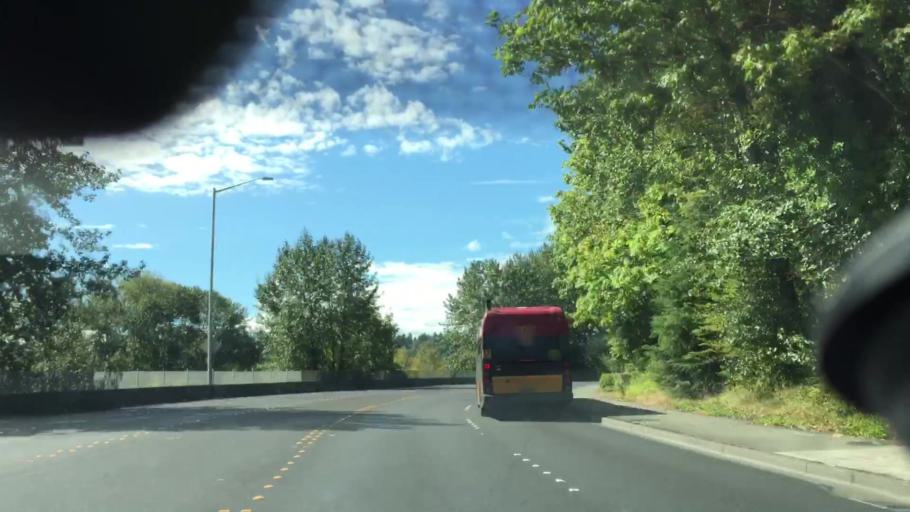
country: US
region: Washington
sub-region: King County
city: Tukwila
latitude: 47.4624
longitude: -122.2535
